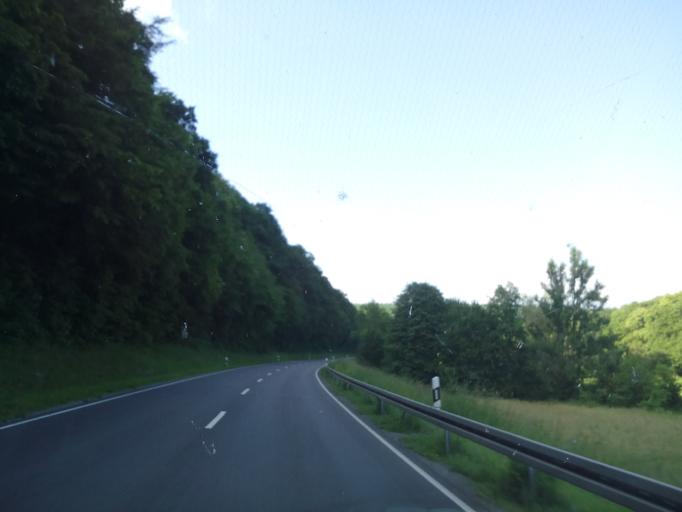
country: DE
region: Bavaria
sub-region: Regierungsbezirk Unterfranken
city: Euerdorf
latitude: 50.1641
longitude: 10.0415
